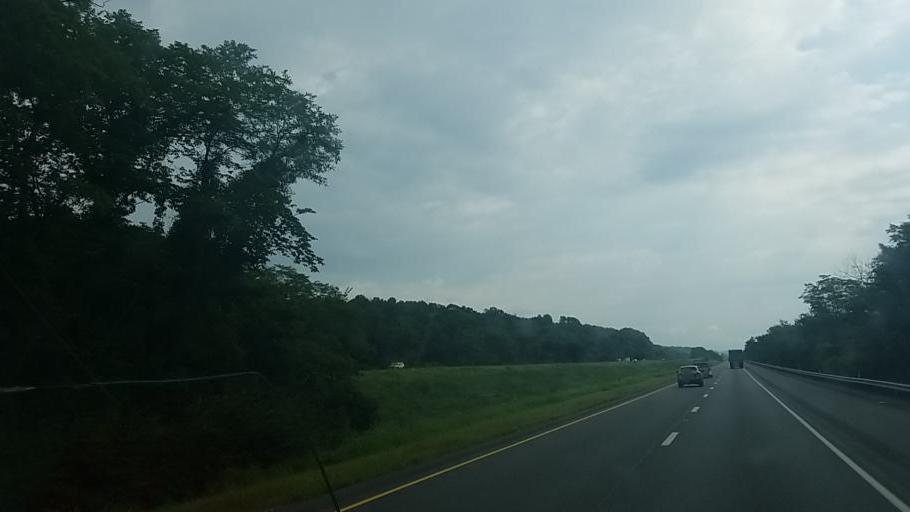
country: US
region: Pennsylvania
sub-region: Juniata County
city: Mifflintown
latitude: 40.5548
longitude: -77.2952
